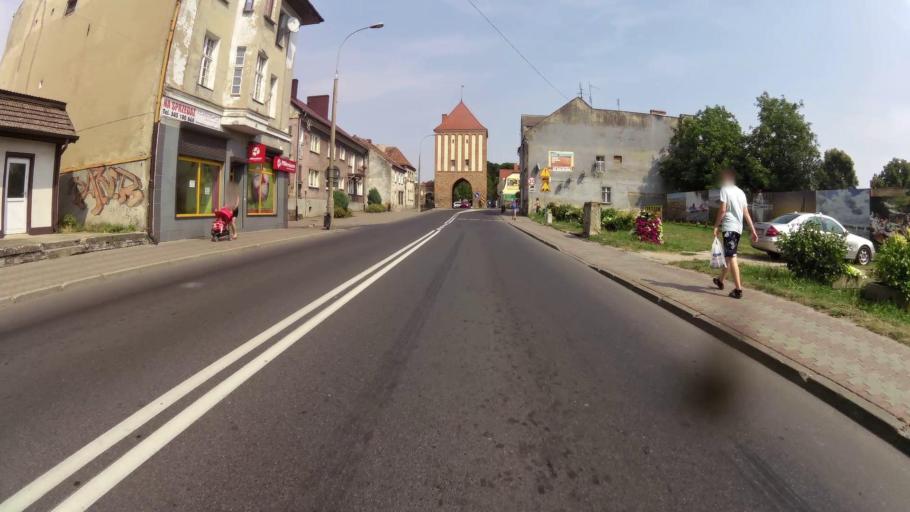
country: PL
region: West Pomeranian Voivodeship
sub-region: Powiat mysliborski
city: Mysliborz
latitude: 52.9246
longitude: 14.8706
